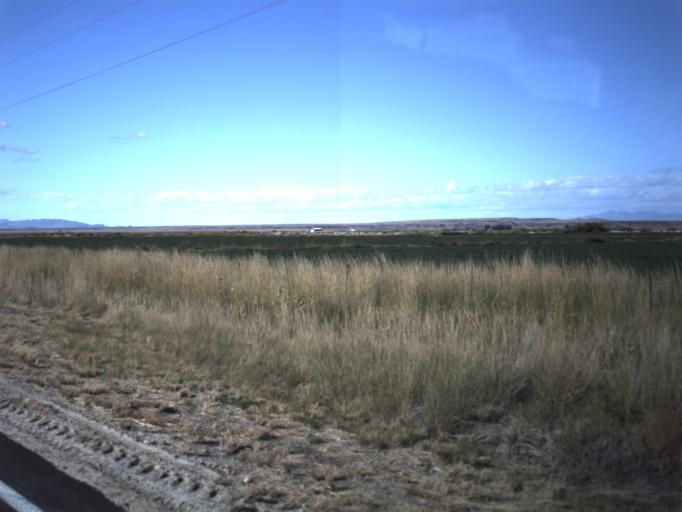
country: US
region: Utah
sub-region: Millard County
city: Delta
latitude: 39.2473
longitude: -112.6586
